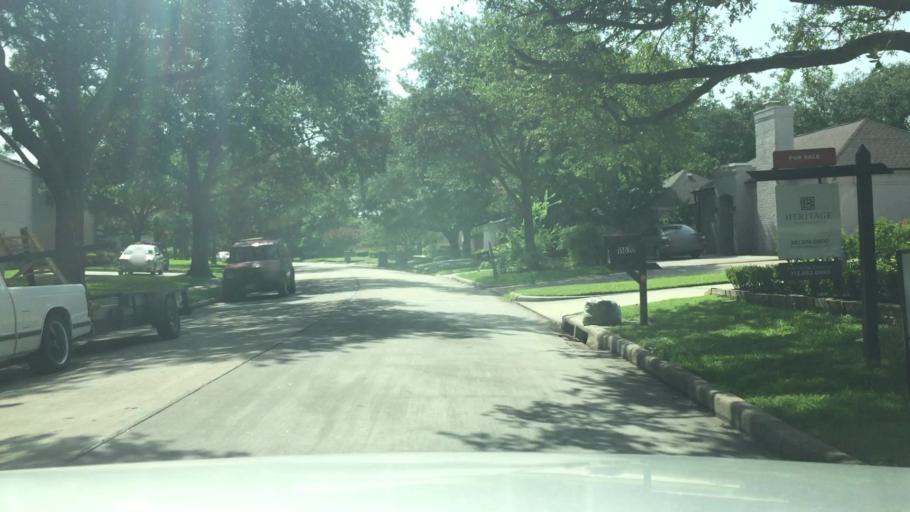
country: US
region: Texas
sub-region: Harris County
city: Bunker Hill Village
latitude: 29.7540
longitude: -95.5821
